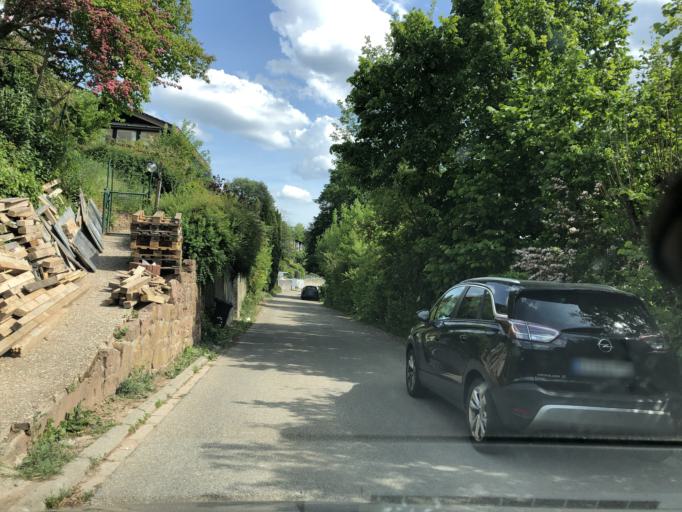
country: DE
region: Baden-Wuerttemberg
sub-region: Karlsruhe Region
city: Schonau
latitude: 49.4377
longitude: 8.8011
